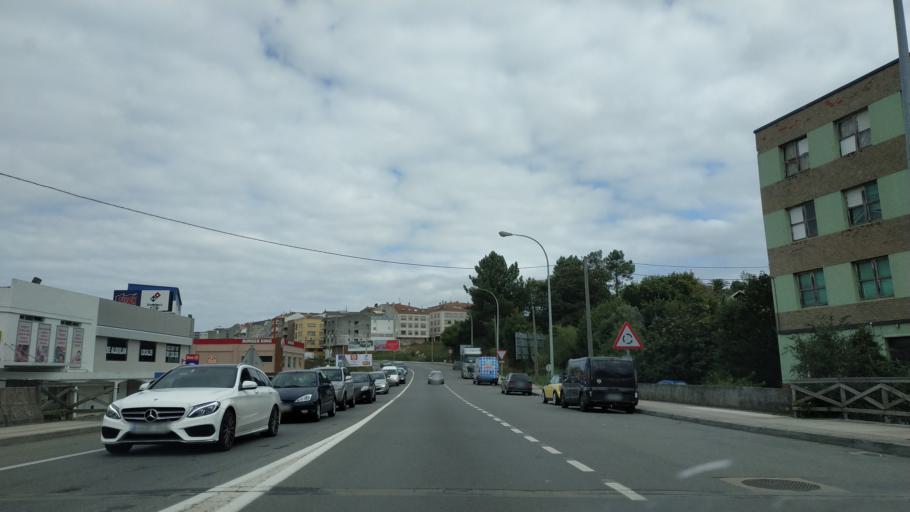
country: ES
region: Galicia
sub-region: Provincia da Coruna
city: Arteixo
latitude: 43.3066
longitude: -8.5067
